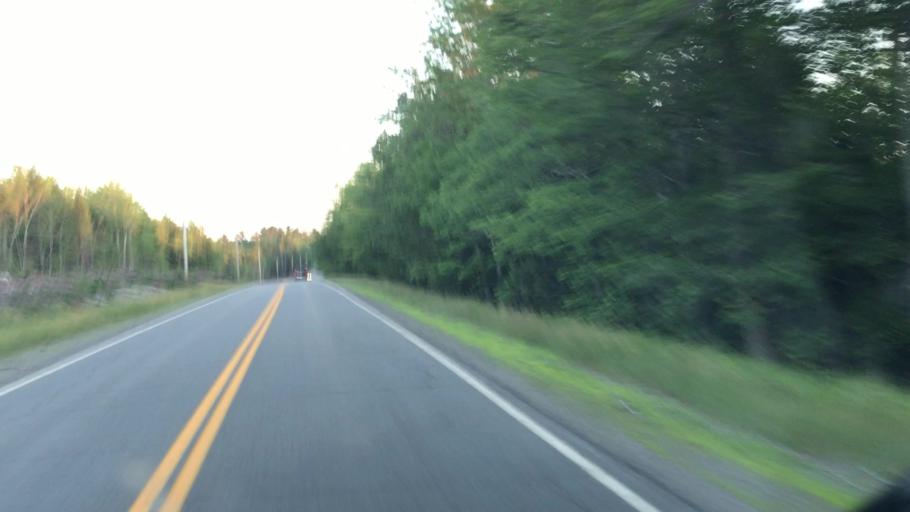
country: US
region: Maine
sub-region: Penobscot County
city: Medway
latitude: 45.5926
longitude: -68.3124
